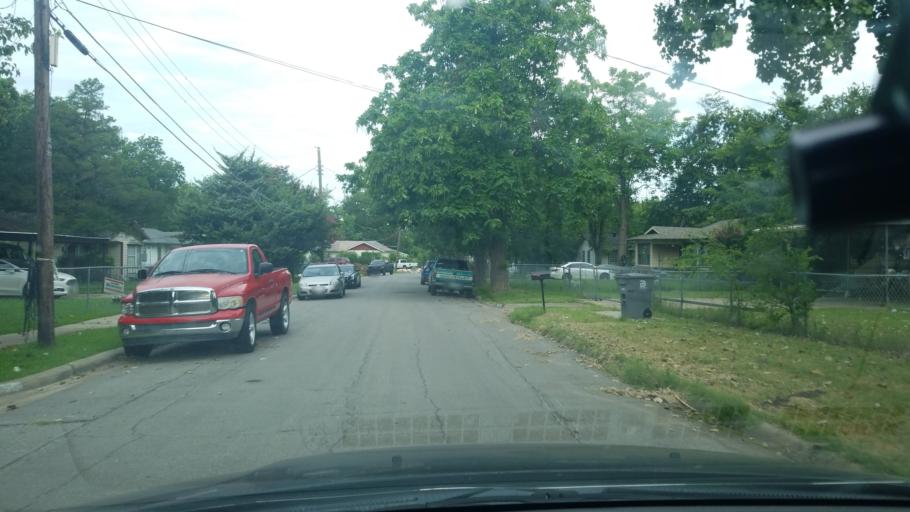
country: US
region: Texas
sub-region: Dallas County
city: Balch Springs
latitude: 32.7379
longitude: -96.6597
